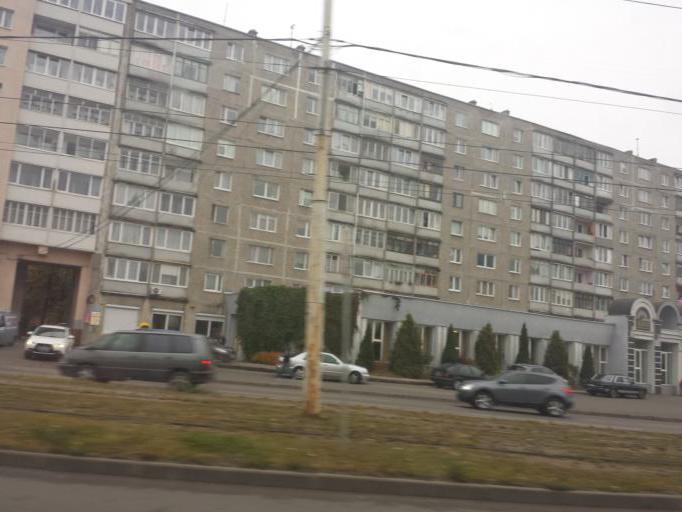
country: RU
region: Kaliningrad
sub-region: Gorod Kaliningrad
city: Kaliningrad
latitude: 54.7113
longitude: 20.5170
